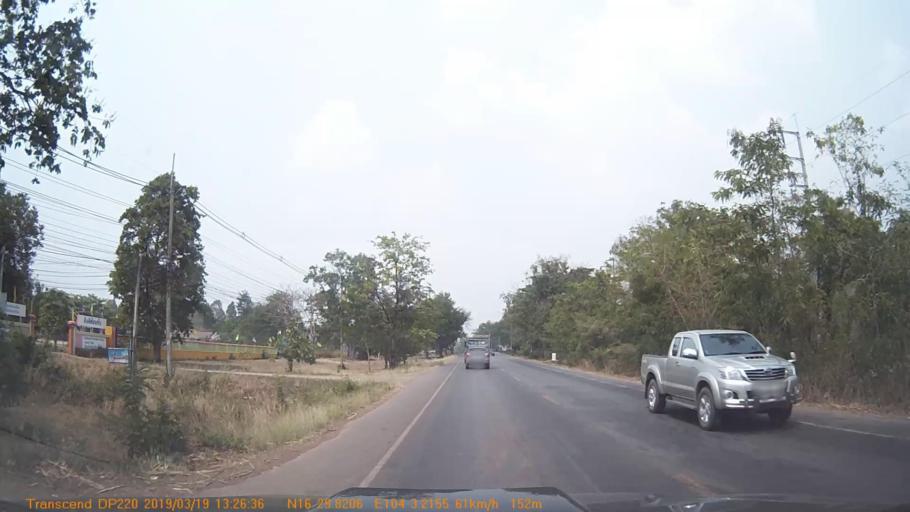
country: TH
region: Kalasin
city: Kuchinarai
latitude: 16.4973
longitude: 104.0537
